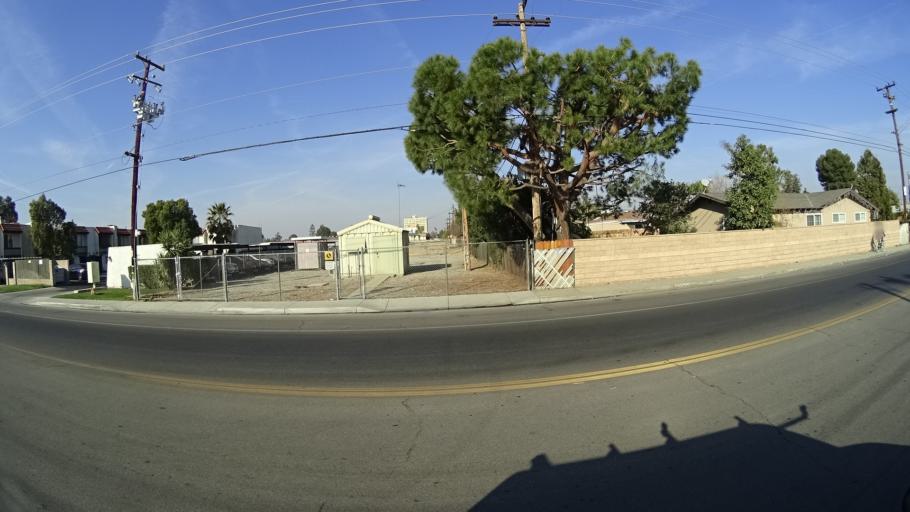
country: US
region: California
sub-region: Kern County
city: Bakersfield
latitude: 35.3251
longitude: -119.0358
